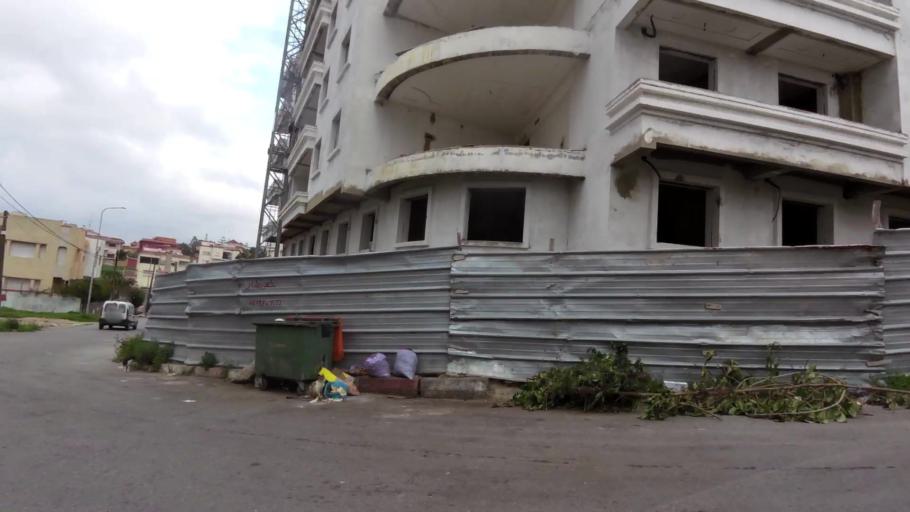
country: MA
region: Tanger-Tetouan
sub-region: Tanger-Assilah
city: Tangier
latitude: 35.7659
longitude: -5.8005
